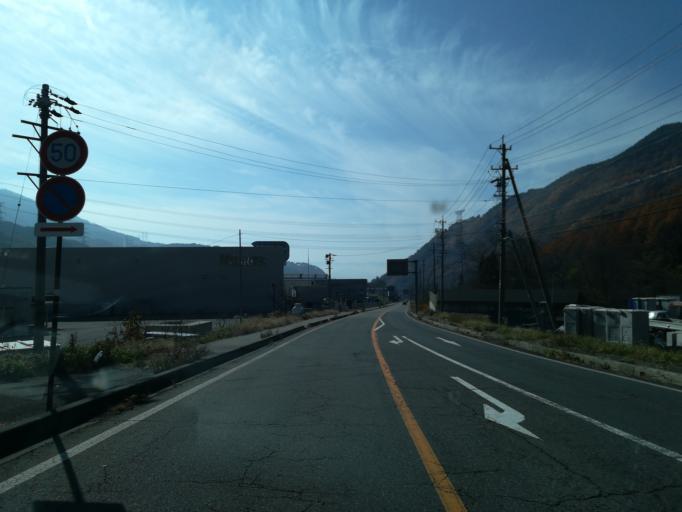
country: JP
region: Nagano
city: Ueda
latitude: 36.4604
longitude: 138.3391
